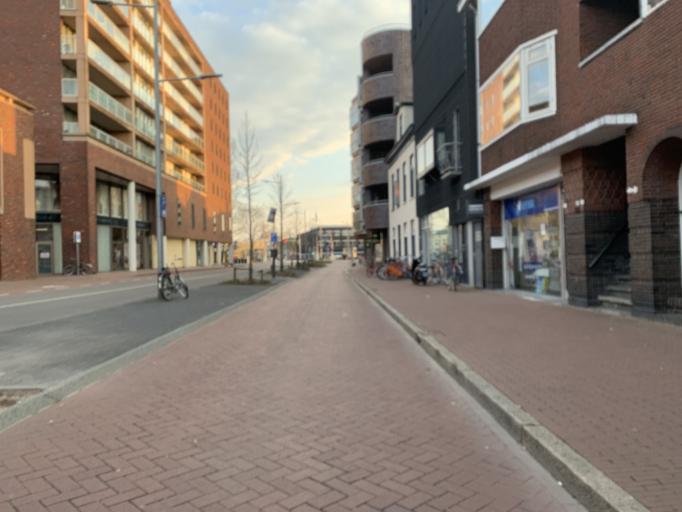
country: NL
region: Groningen
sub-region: Gemeente Groningen
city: Groningen
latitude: 53.2153
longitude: 6.5565
